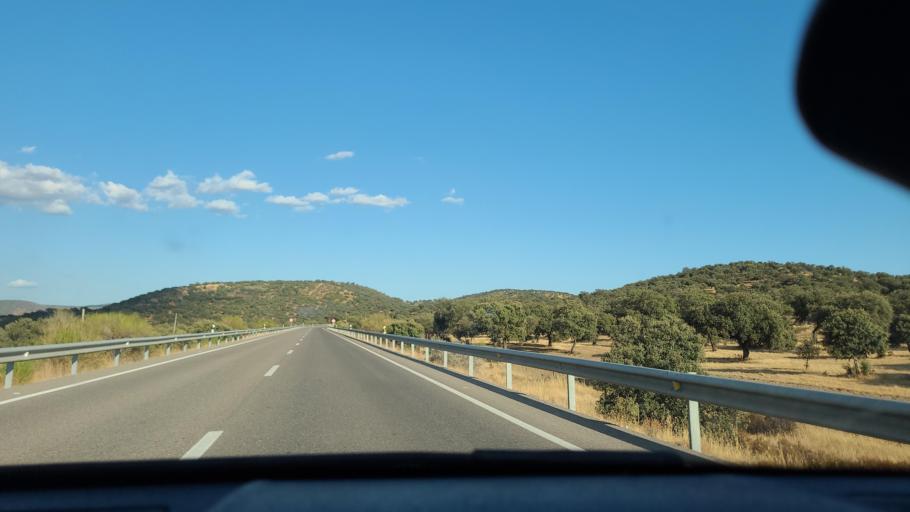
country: ES
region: Andalusia
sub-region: Province of Cordoba
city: Espiel
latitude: 38.2028
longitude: -5.1110
